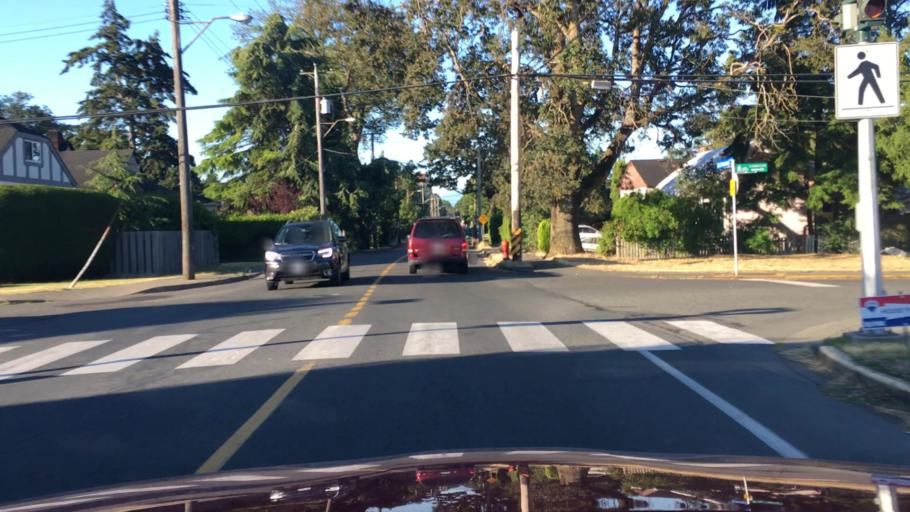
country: CA
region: British Columbia
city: Oak Bay
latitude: 48.4389
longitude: -123.3281
